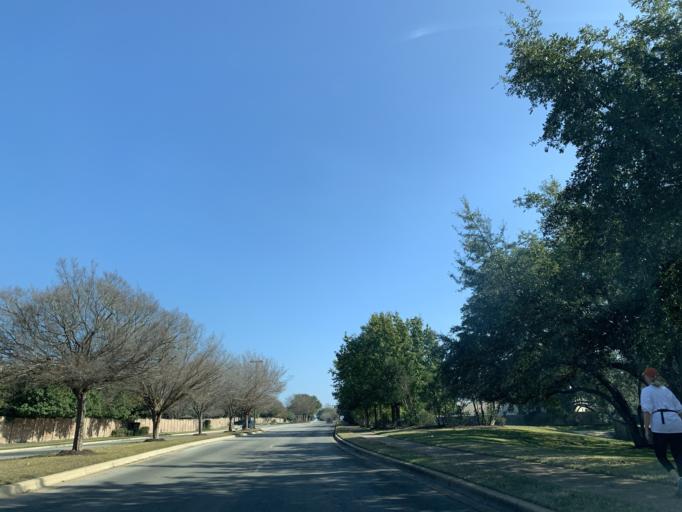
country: US
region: Texas
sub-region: Travis County
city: Windemere
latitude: 30.5082
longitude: -97.6183
